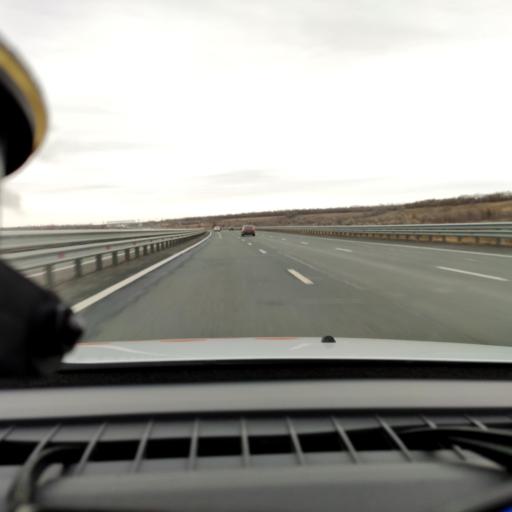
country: RU
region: Samara
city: Smyshlyayevka
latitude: 53.1510
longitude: 50.3600
